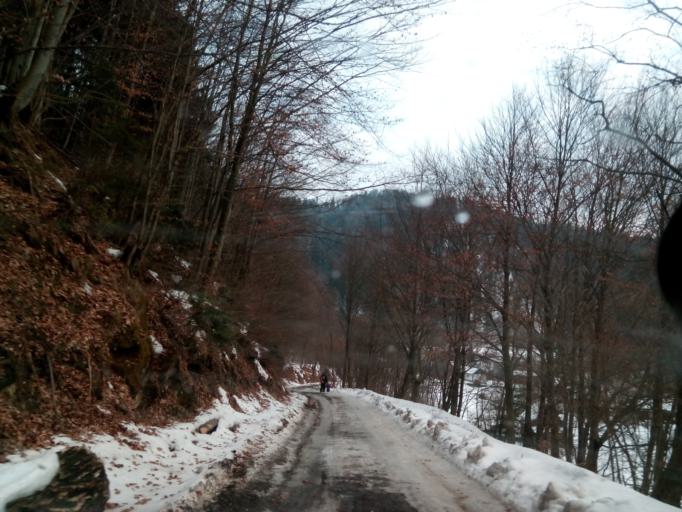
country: SK
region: Presovsky
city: Sabinov
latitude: 49.1963
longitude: 21.0885
